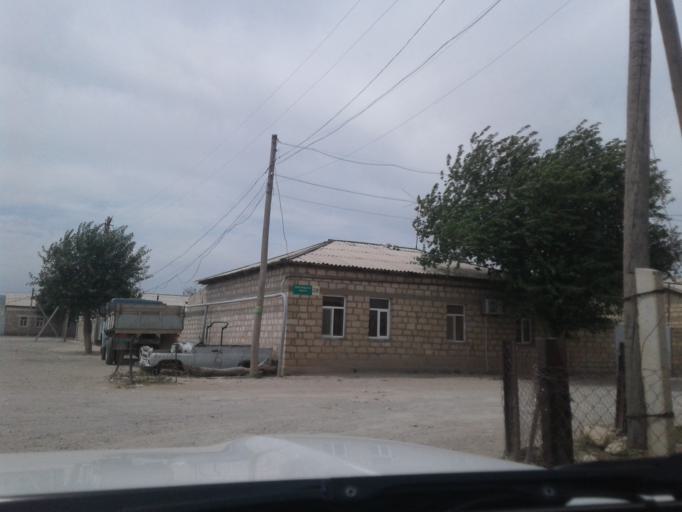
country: TM
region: Balkan
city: Serdar
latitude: 38.9899
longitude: 56.2682
